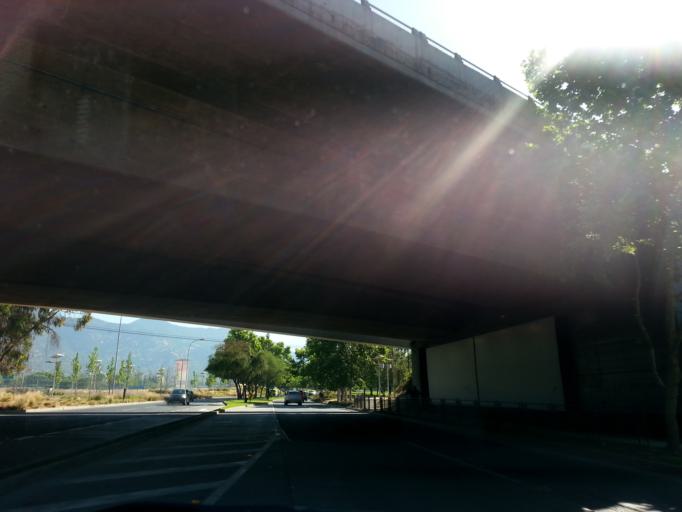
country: CL
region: Santiago Metropolitan
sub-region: Provincia de Santiago
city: Villa Presidente Frei, Nunoa, Santiago, Chile
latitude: -33.3904
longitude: -70.5983
